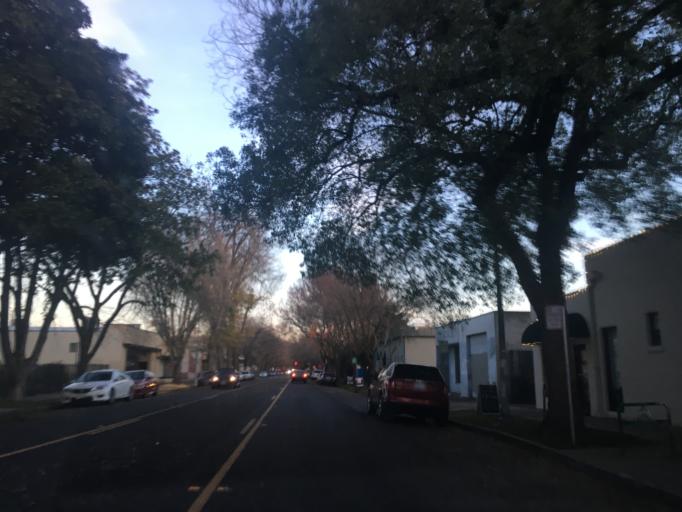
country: US
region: California
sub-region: Sacramento County
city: Sacramento
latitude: 38.5697
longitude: -121.4951
